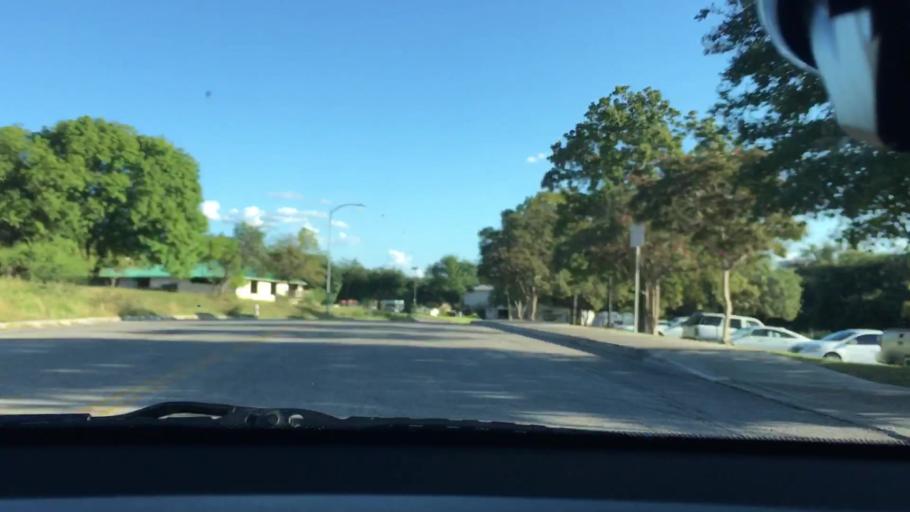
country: US
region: Texas
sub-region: Bexar County
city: Balcones Heights
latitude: 29.5204
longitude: -98.5752
